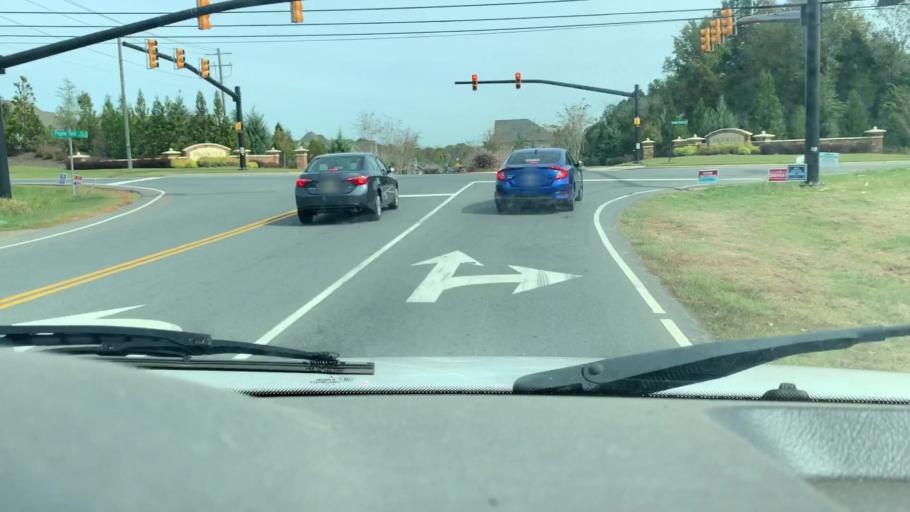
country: US
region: North Carolina
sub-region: Mecklenburg County
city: Huntersville
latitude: 35.4241
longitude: -80.7554
